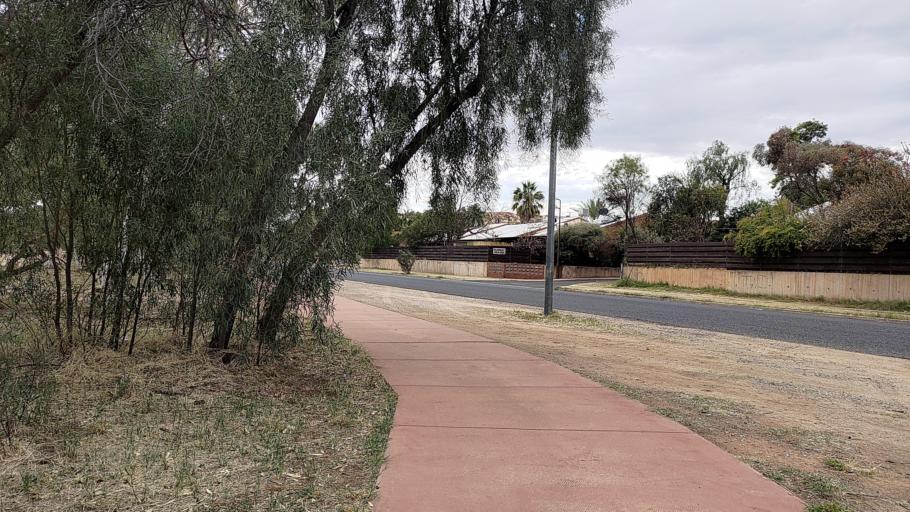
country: AU
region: Northern Territory
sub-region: Alice Springs
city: Alice Springs
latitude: -23.7088
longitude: 133.8812
